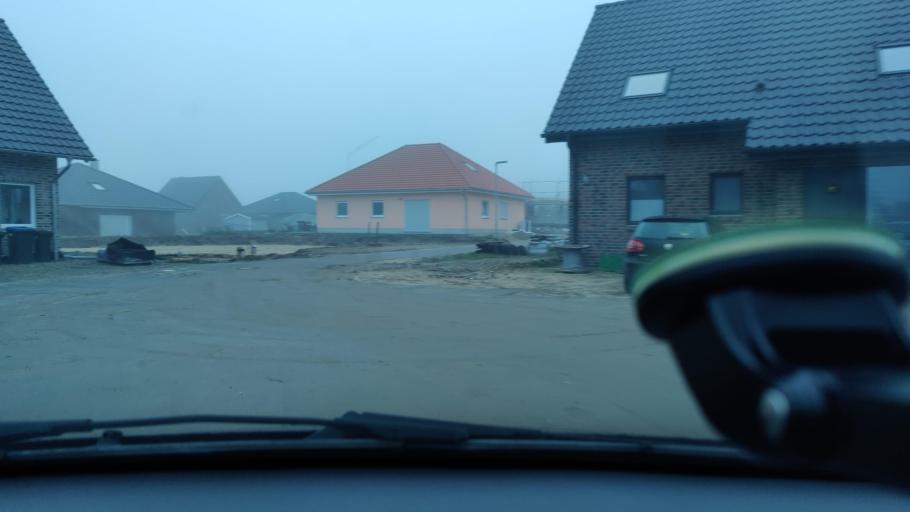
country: DE
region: North Rhine-Westphalia
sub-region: Regierungsbezirk Dusseldorf
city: Kleve
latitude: 51.7679
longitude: 6.2053
